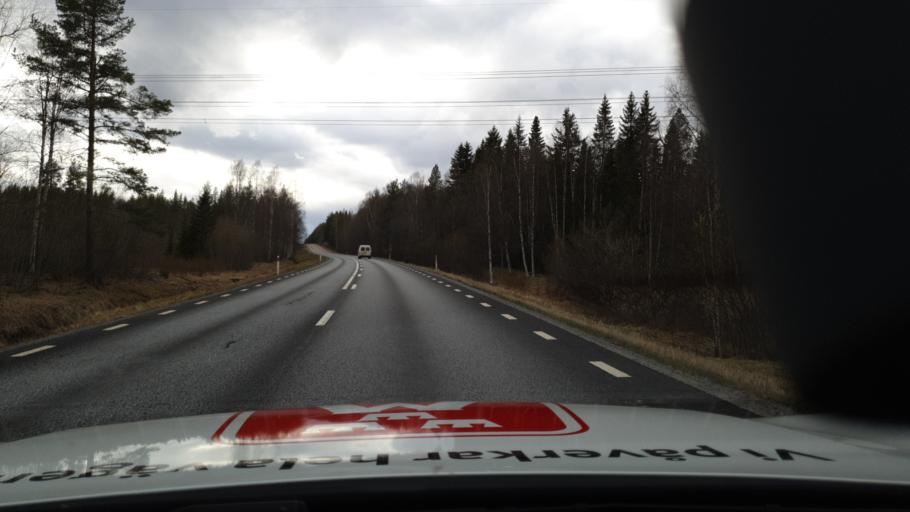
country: SE
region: Jaemtland
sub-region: OEstersunds Kommun
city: Brunflo
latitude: 63.1933
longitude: 15.1663
